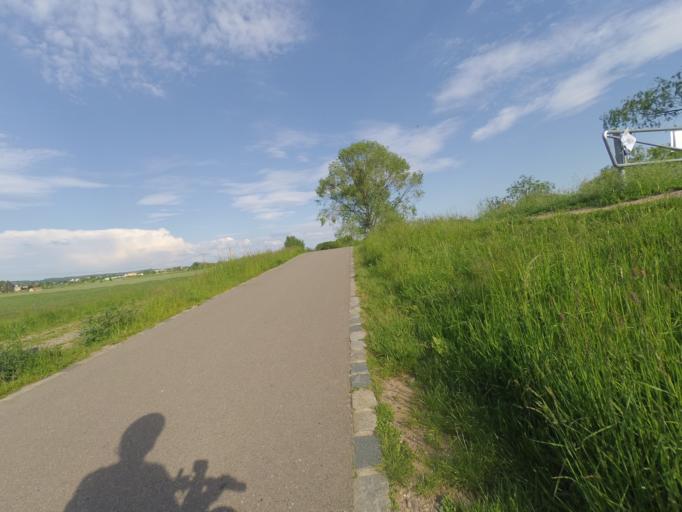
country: DE
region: Saxony
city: Radebeul
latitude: 51.0981
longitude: 13.6416
